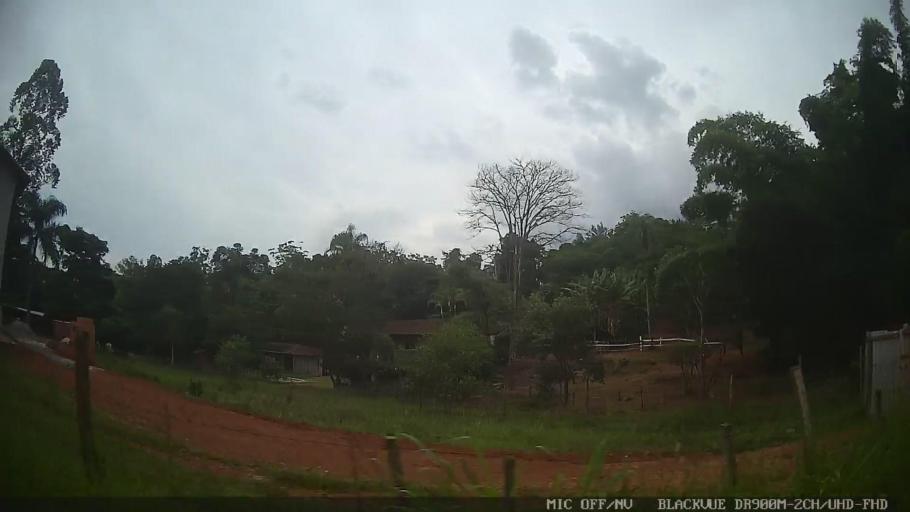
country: BR
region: Sao Paulo
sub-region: Atibaia
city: Atibaia
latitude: -23.1584
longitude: -46.6033
